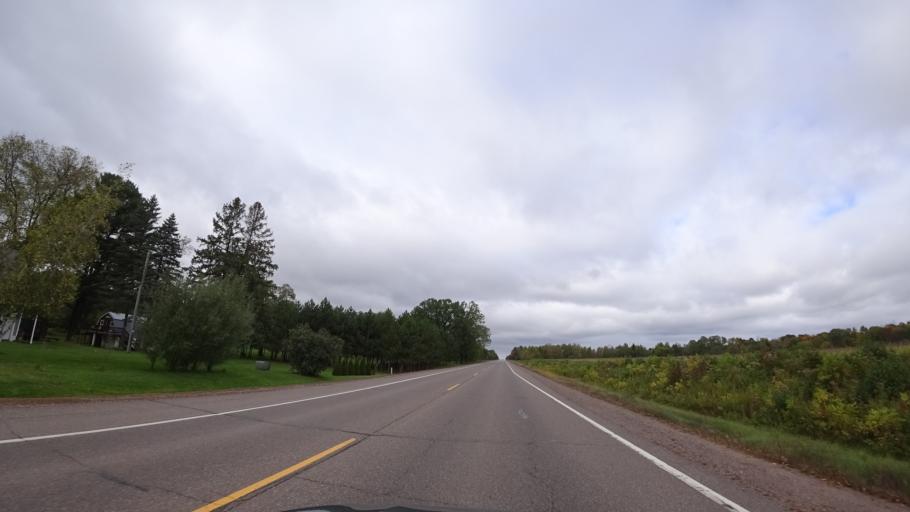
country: US
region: Wisconsin
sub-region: Rusk County
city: Ladysmith
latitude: 45.5092
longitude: -91.1115
